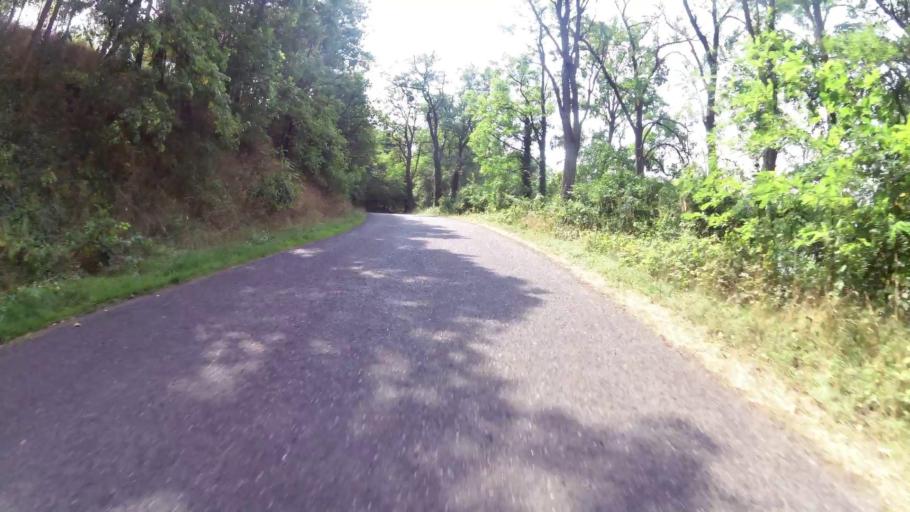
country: PL
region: West Pomeranian Voivodeship
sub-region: Powiat gryfinski
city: Moryn
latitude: 52.8480
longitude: 14.4008
